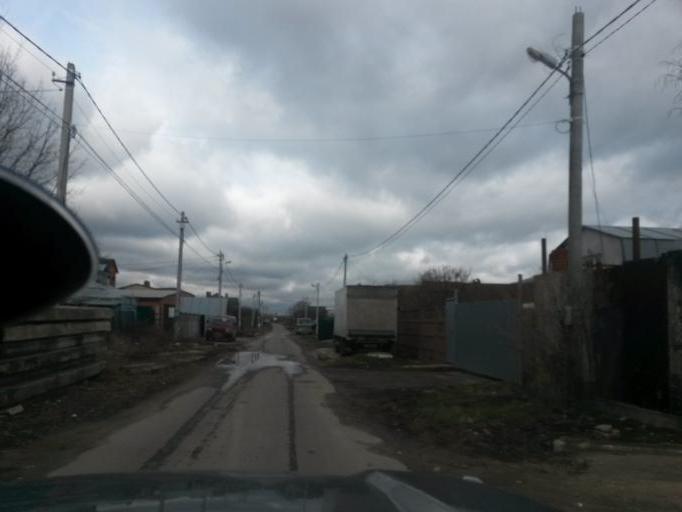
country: RU
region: Moskovskaya
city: Kotel'niki
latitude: 55.6029
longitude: 37.8259
